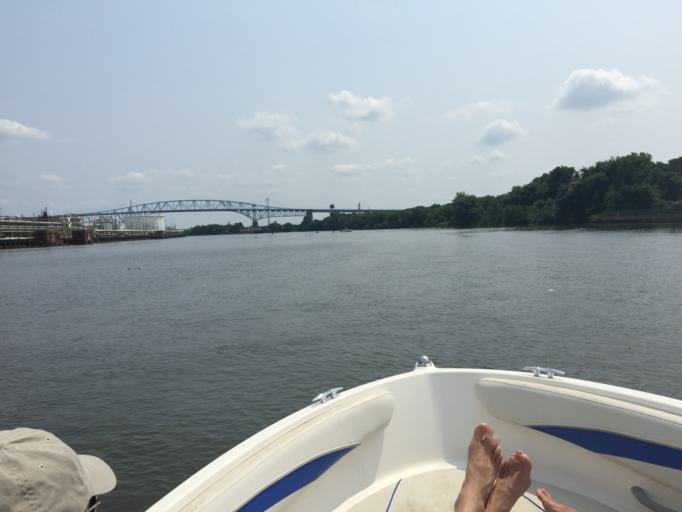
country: US
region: Pennsylvania
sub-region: Delaware County
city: Colwyn
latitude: 39.9065
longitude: -75.2158
